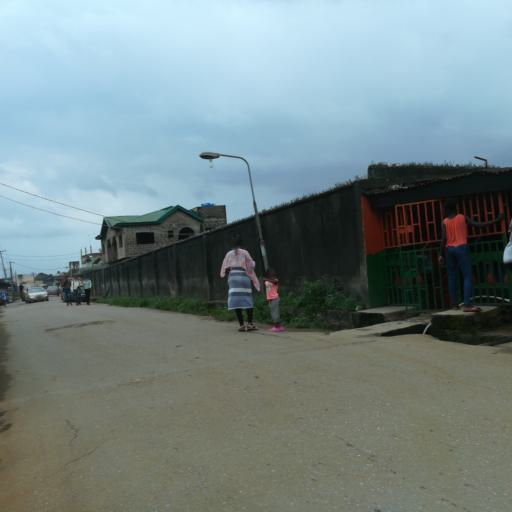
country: NG
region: Lagos
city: Agege
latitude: 6.6034
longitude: 3.2956
